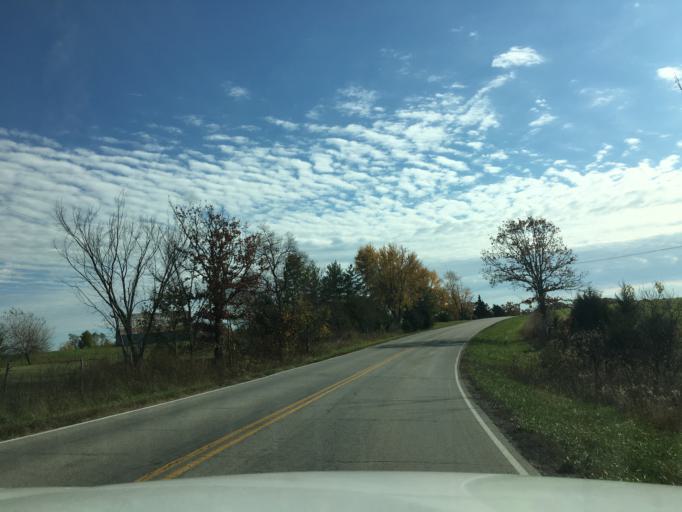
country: US
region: Missouri
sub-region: Maries County
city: Belle
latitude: 38.3225
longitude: -91.7550
